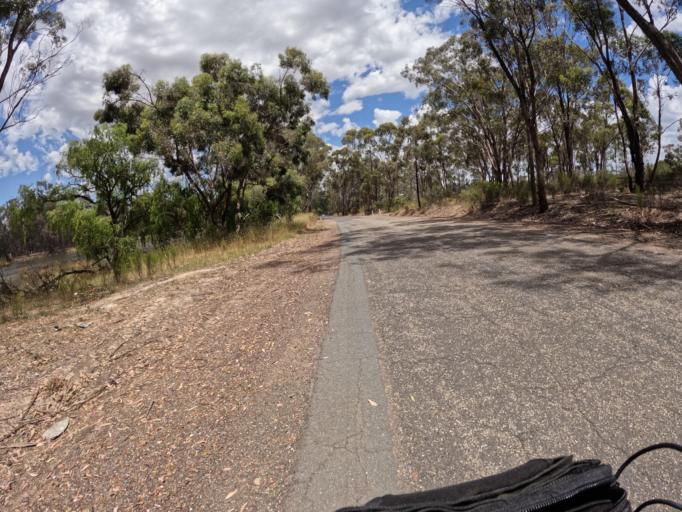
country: AU
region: Victoria
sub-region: Greater Shepparton
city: Shepparton
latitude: -36.6929
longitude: 145.1746
